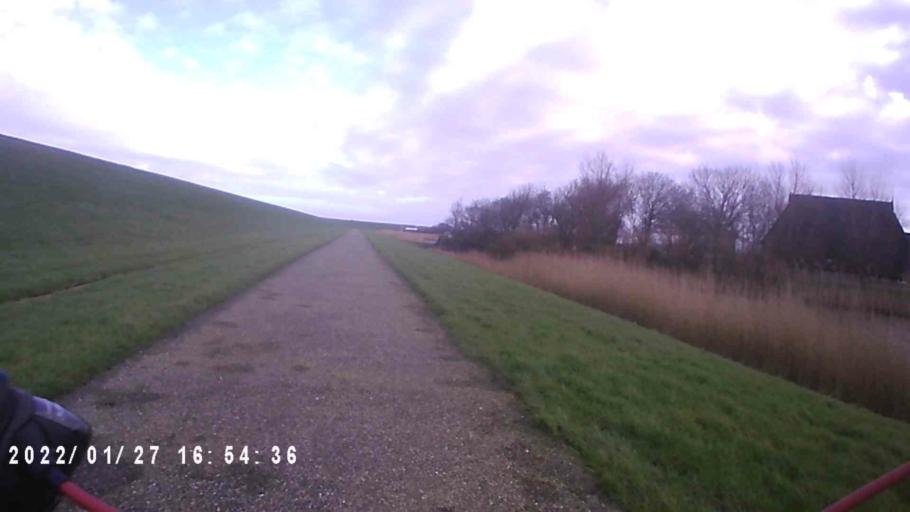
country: NL
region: Friesland
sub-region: Gemeente Dongeradeel
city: Anjum
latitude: 53.4060
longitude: 6.0623
